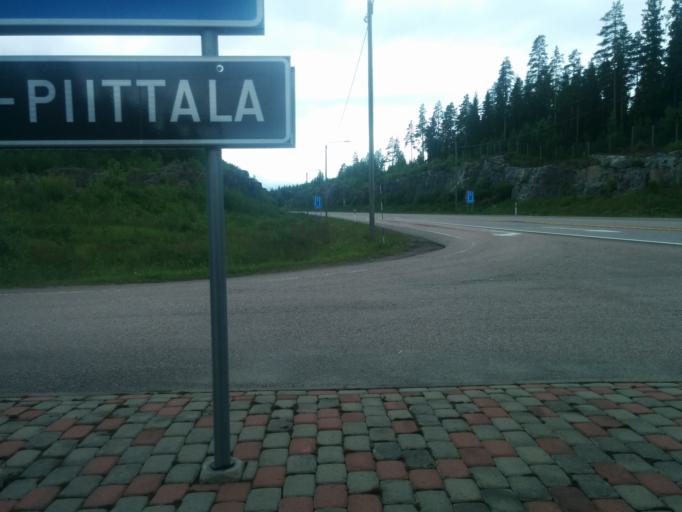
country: FI
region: Pirkanmaa
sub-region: Tampere
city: Kuhmalahti
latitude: 61.7075
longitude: 24.5687
